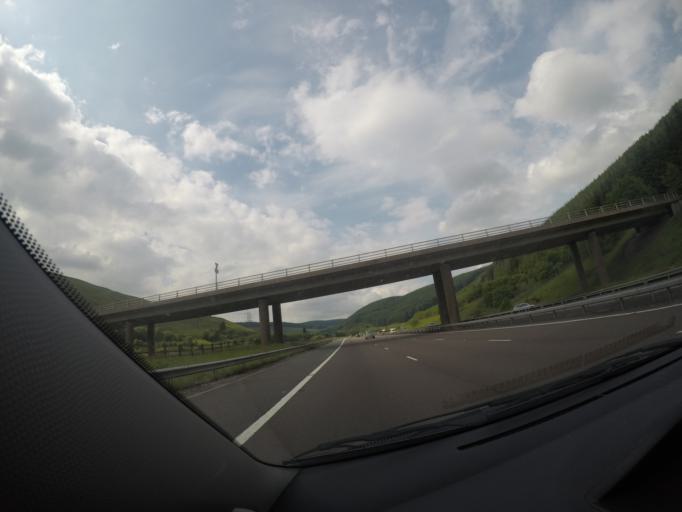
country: GB
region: Scotland
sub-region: Dumfries and Galloway
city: Moffat
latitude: 55.3853
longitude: -3.5215
